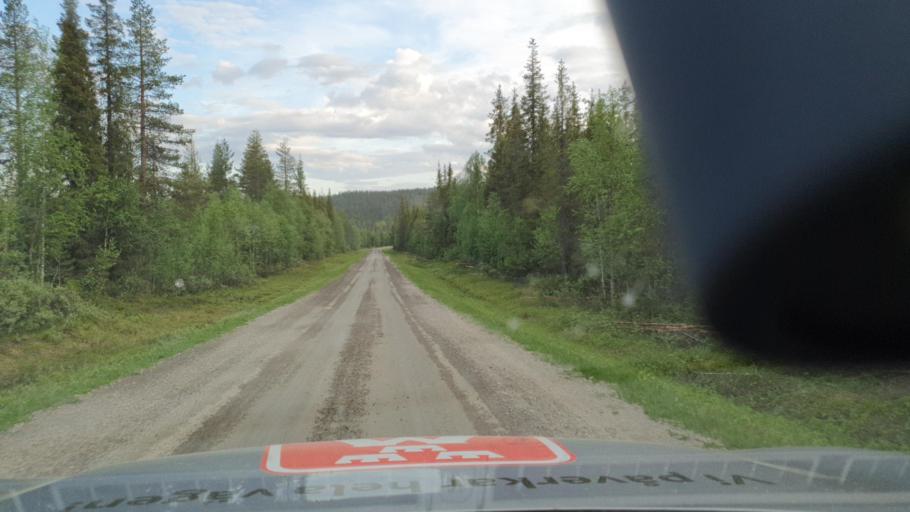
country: SE
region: Norrbotten
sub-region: Bodens Kommun
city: Boden
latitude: 66.6104
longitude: 21.3537
